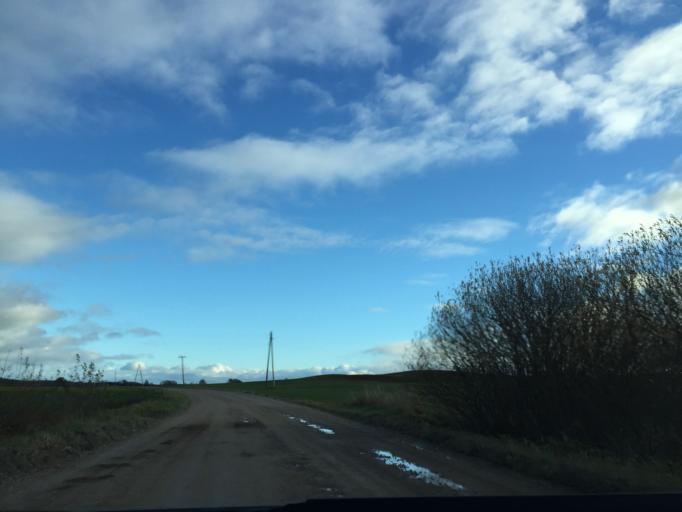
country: LV
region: Jaunpils
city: Jaunpils
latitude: 56.9215
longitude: 22.9507
